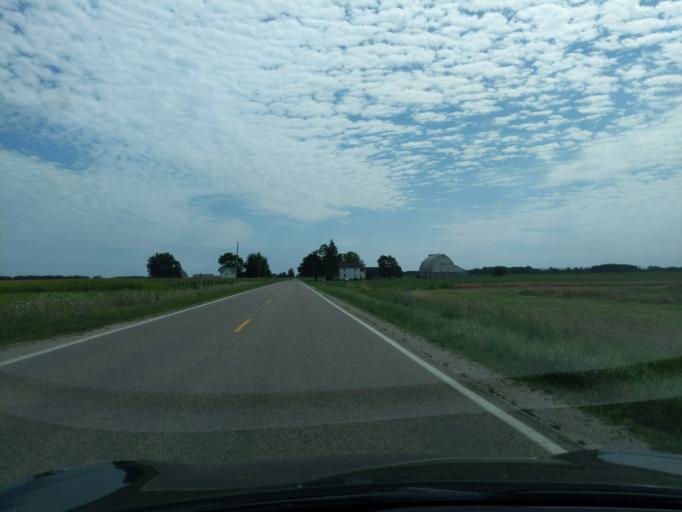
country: US
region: Michigan
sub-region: Gratiot County
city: Breckenridge
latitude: 43.2918
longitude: -84.4600
